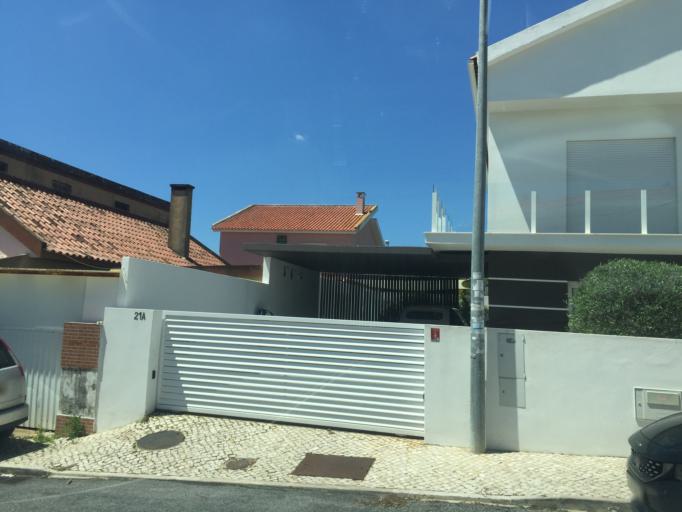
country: PT
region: Lisbon
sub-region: Oeiras
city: Quejas
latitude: 38.7233
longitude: -9.2630
